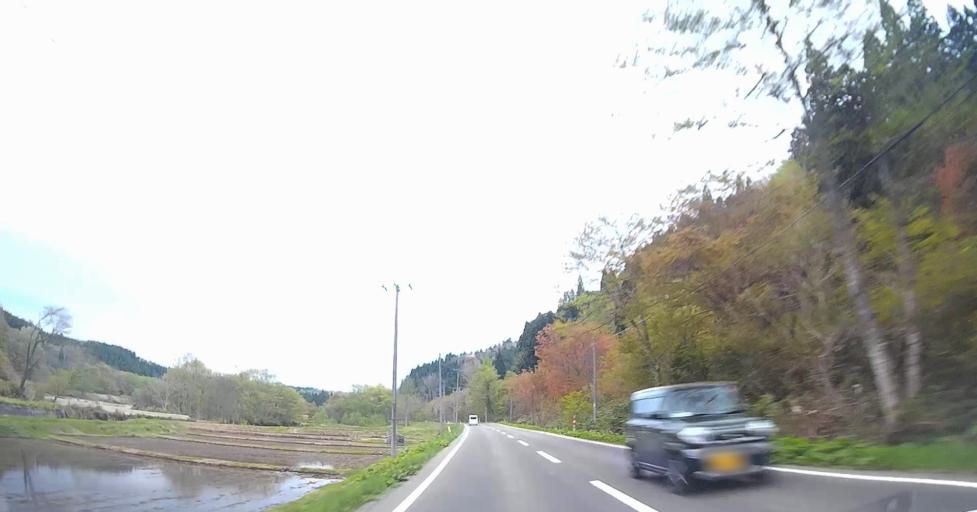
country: JP
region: Aomori
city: Goshogawara
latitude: 41.1250
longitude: 140.5197
